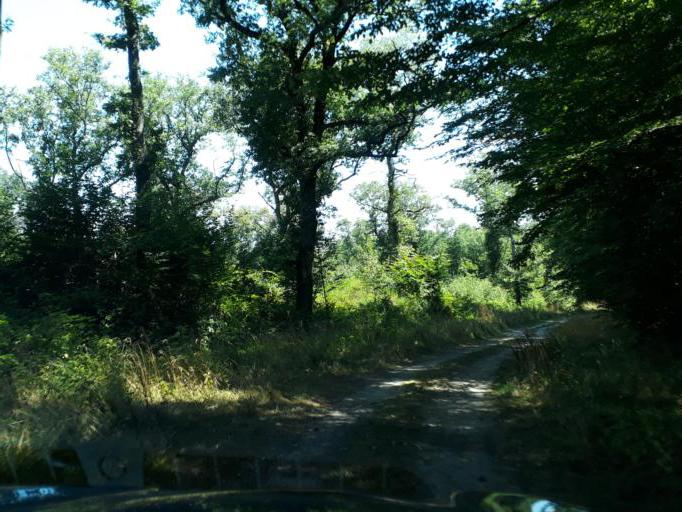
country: FR
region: Centre
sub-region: Departement du Loiret
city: Chevilly
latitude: 47.9915
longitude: 1.8936
